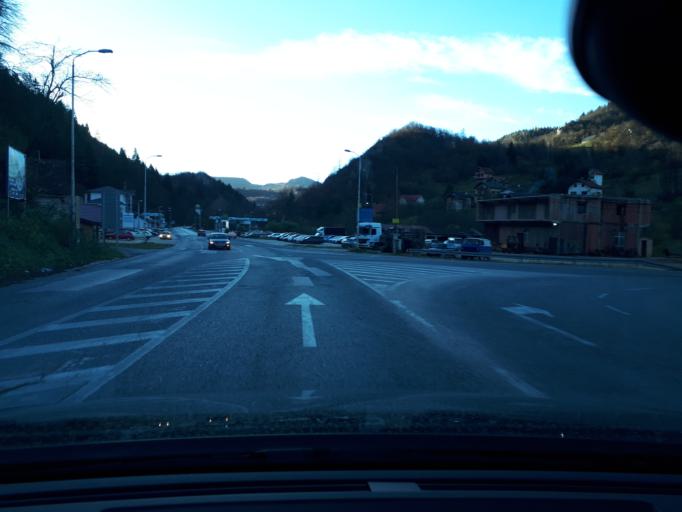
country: BA
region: Republika Srpska
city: Pale
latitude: 43.8507
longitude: 18.5413
